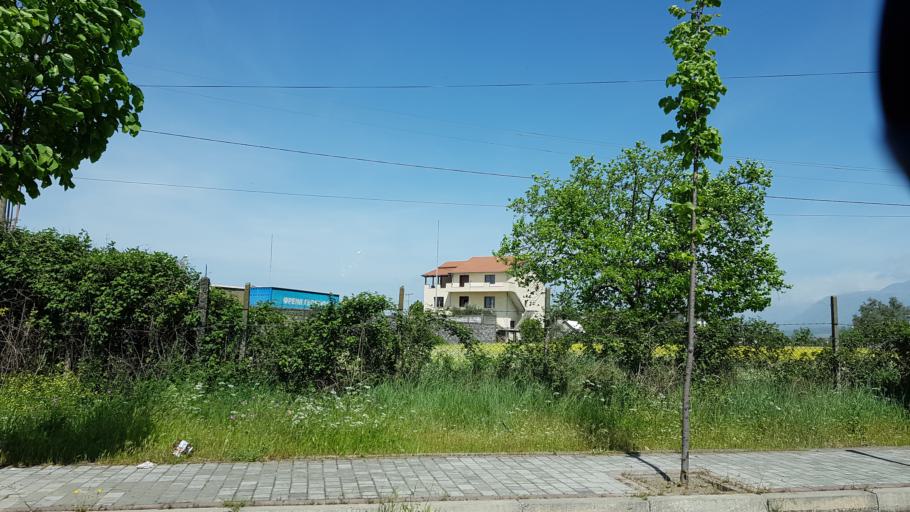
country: AL
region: Shkoder
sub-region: Rrethi i Shkodres
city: Shkoder
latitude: 42.0974
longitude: 19.5406
